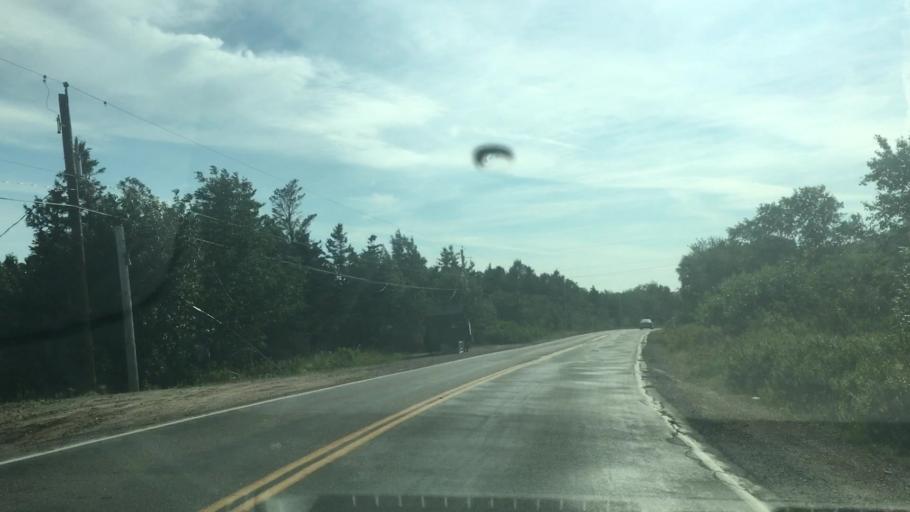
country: CA
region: Nova Scotia
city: Sydney Mines
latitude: 46.8781
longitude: -60.5175
